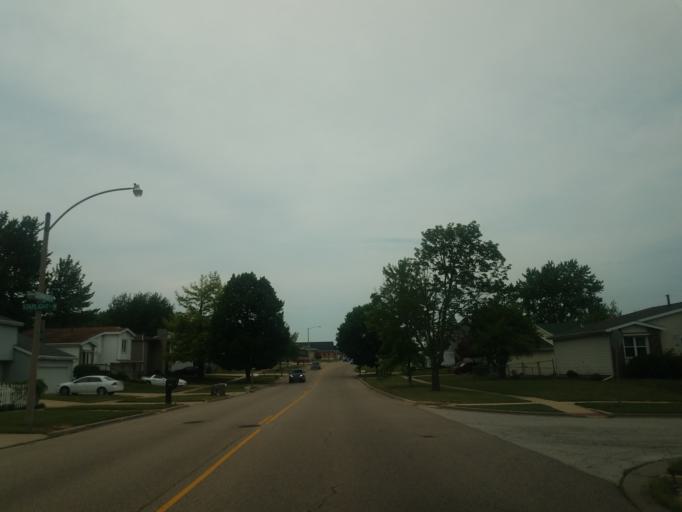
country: US
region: Illinois
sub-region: McLean County
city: Normal
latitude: 40.4962
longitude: -88.9460
